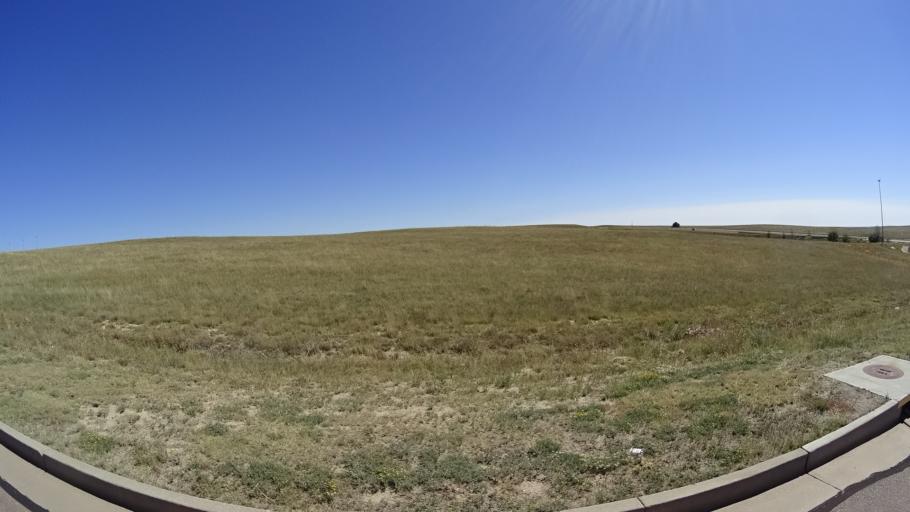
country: US
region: Colorado
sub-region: El Paso County
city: Security-Widefield
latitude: 38.7682
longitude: -104.6987
